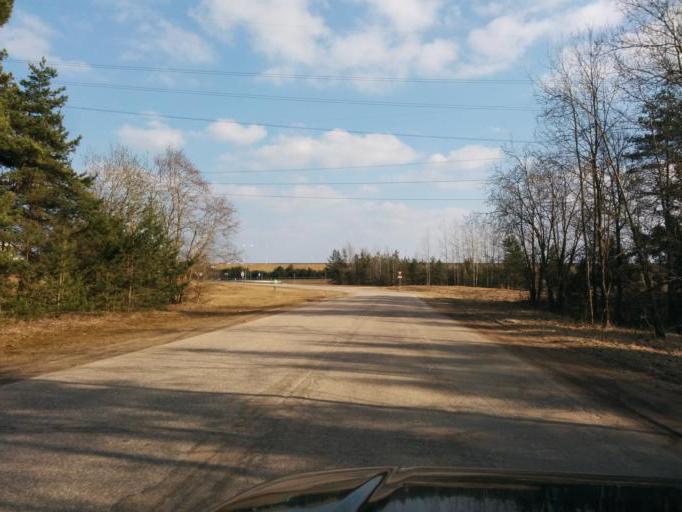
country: LV
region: Kekava
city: Kekava
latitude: 56.8497
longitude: 24.2644
